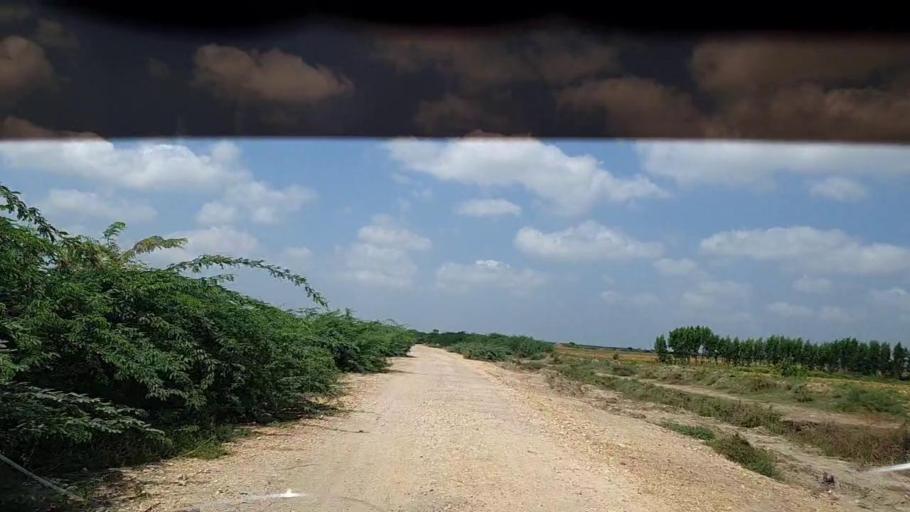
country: PK
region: Sindh
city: Kadhan
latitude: 24.5908
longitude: 68.9675
